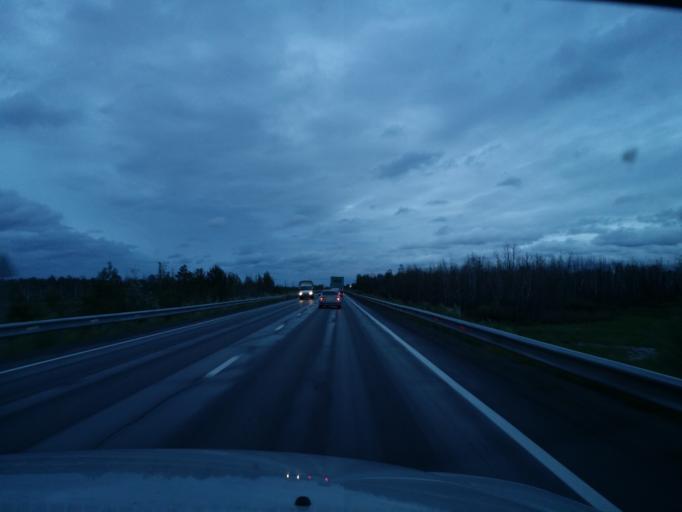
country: RU
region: Khanty-Mansiyskiy Avtonomnyy Okrug
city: Lokosovo
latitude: 61.4550
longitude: 74.6806
